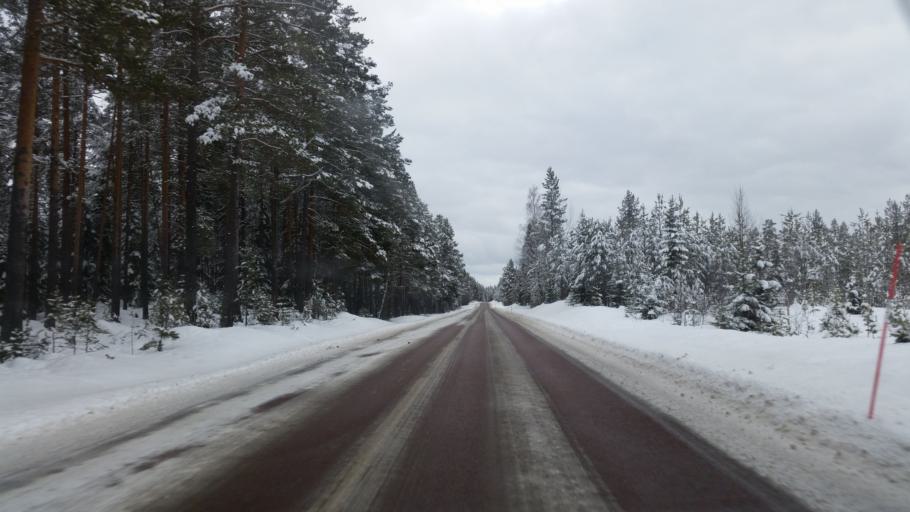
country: SE
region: Jaemtland
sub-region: Harjedalens Kommun
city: Sveg
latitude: 62.3829
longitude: 14.6661
